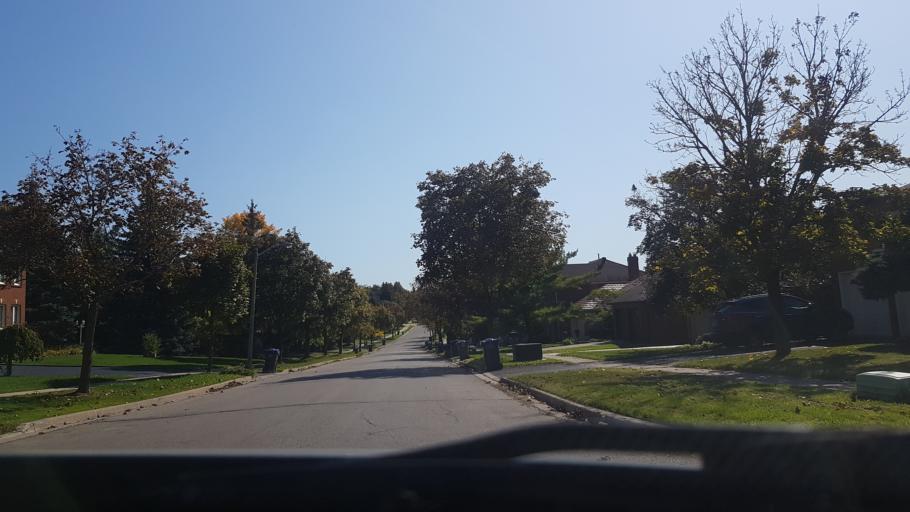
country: CA
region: Ontario
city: Brampton
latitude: 43.7421
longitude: -79.8039
